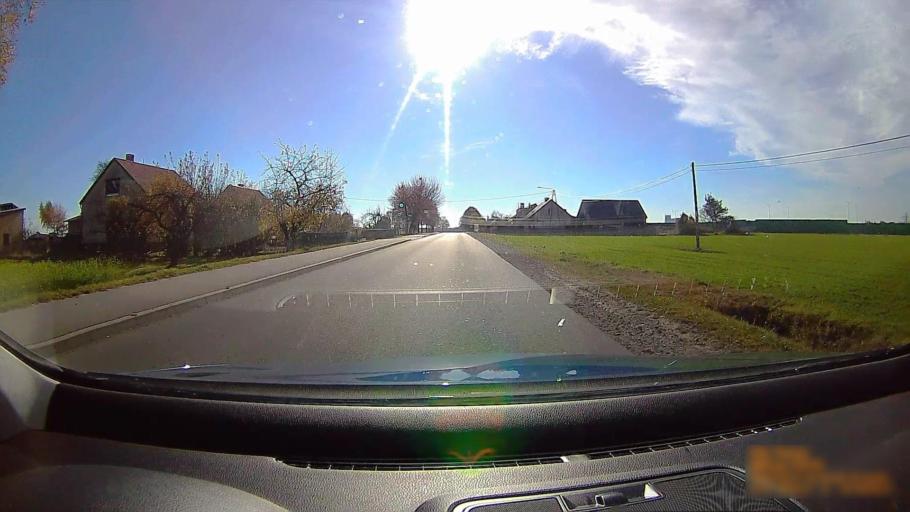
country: PL
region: Greater Poland Voivodeship
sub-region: Powiat kepinski
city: Kepno
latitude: 51.3148
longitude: 18.0142
